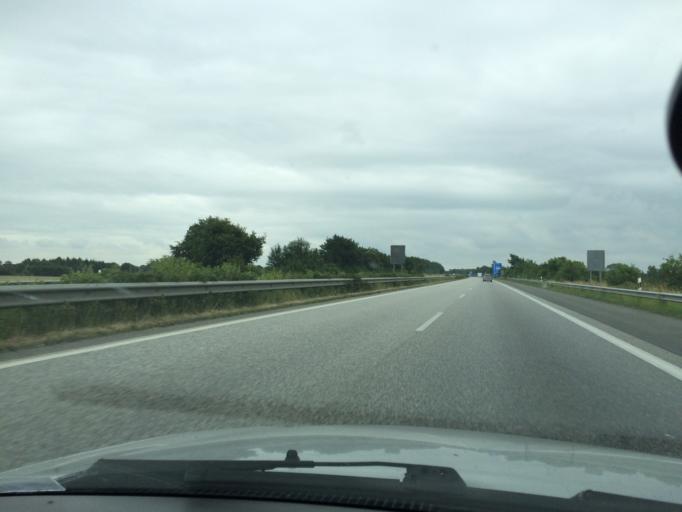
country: DE
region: Schleswig-Holstein
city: Handewitt
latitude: 54.7818
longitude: 9.3404
